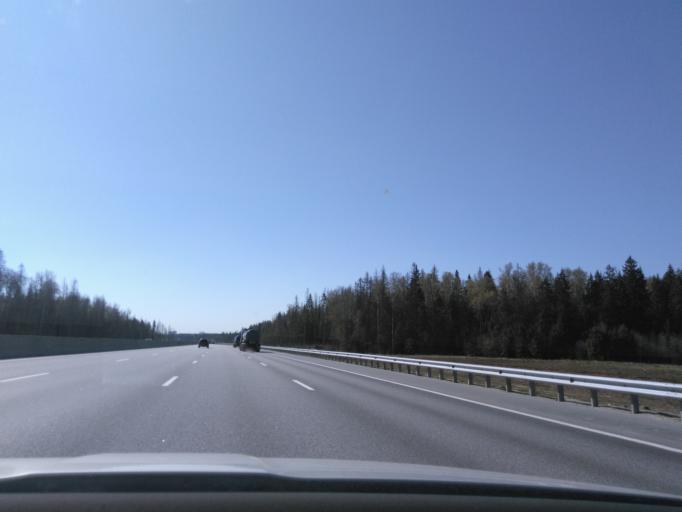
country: RU
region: Moskovskaya
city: Skhodnya
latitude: 55.9955
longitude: 37.2990
